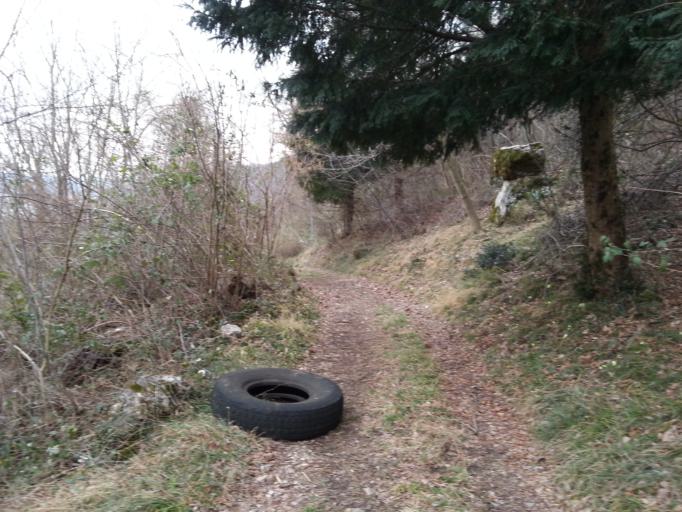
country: CH
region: Ticino
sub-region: Mendrisio District
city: Riva San Vitale
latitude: 45.8993
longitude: 8.9642
